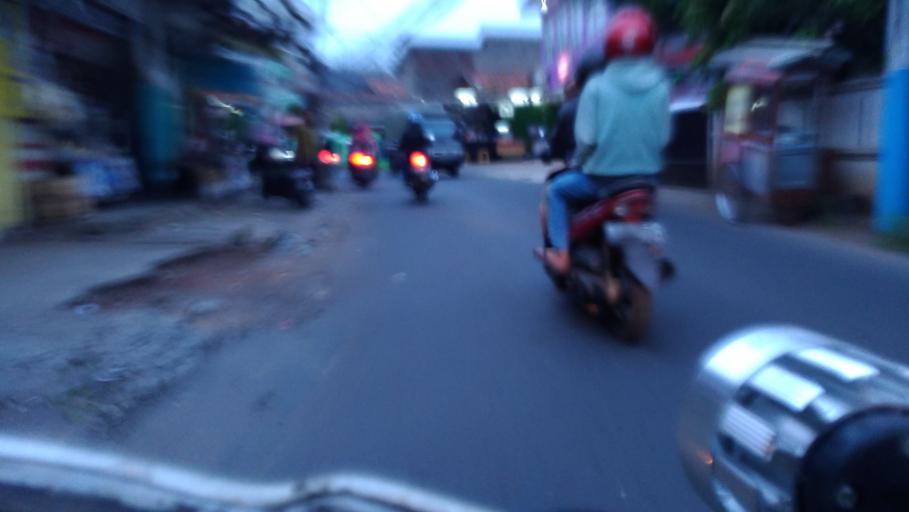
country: ID
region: West Java
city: Depok
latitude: -6.3655
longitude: 106.8860
